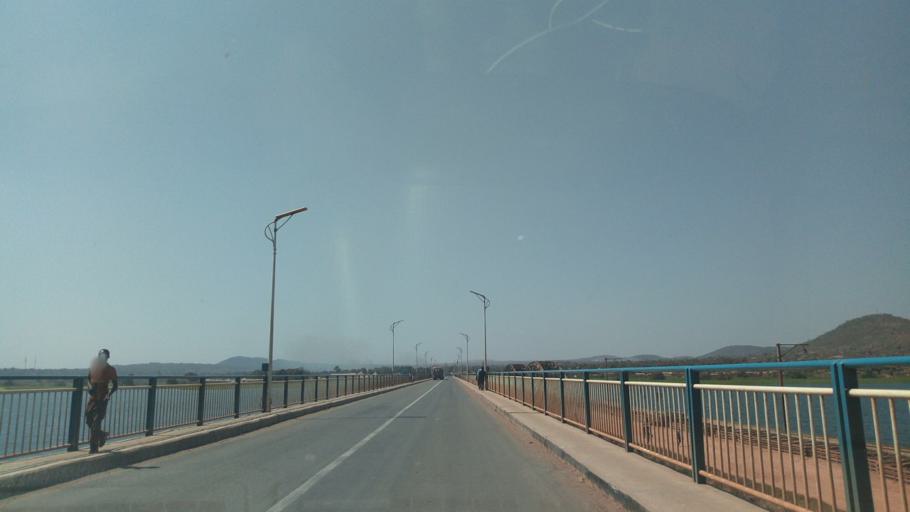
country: CD
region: Katanga
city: Kolwezi
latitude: -10.7811
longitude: 25.7239
